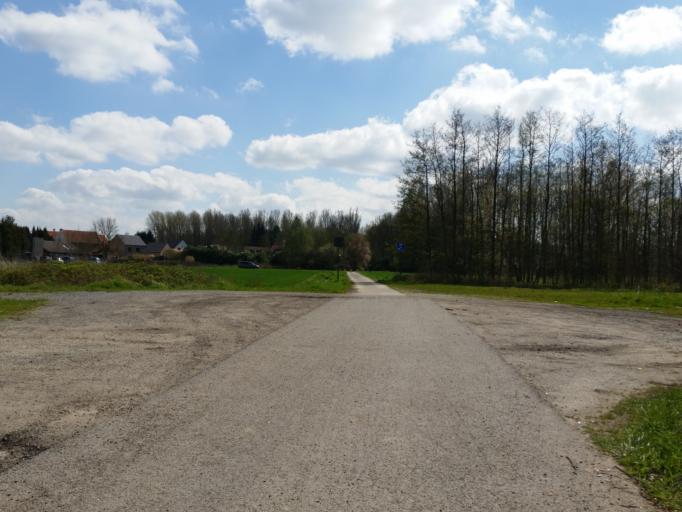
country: BE
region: Flanders
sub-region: Provincie Vlaams-Brabant
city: Kampenhout
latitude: 50.9477
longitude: 4.5797
